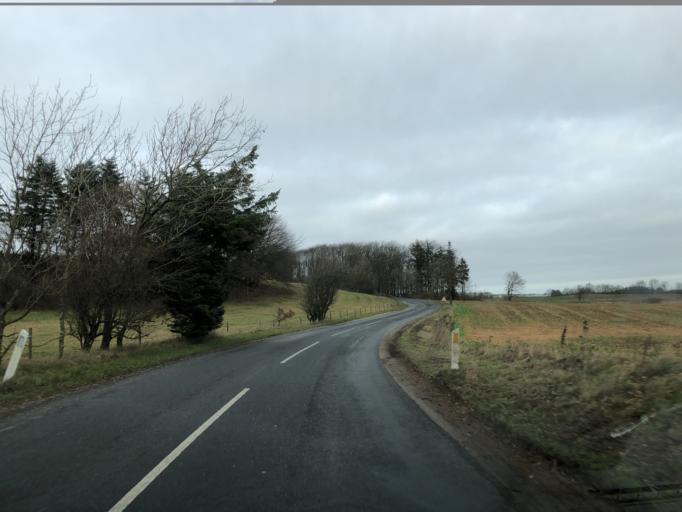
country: DK
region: Central Jutland
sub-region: Viborg Kommune
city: Stoholm
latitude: 56.4375
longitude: 9.1059
